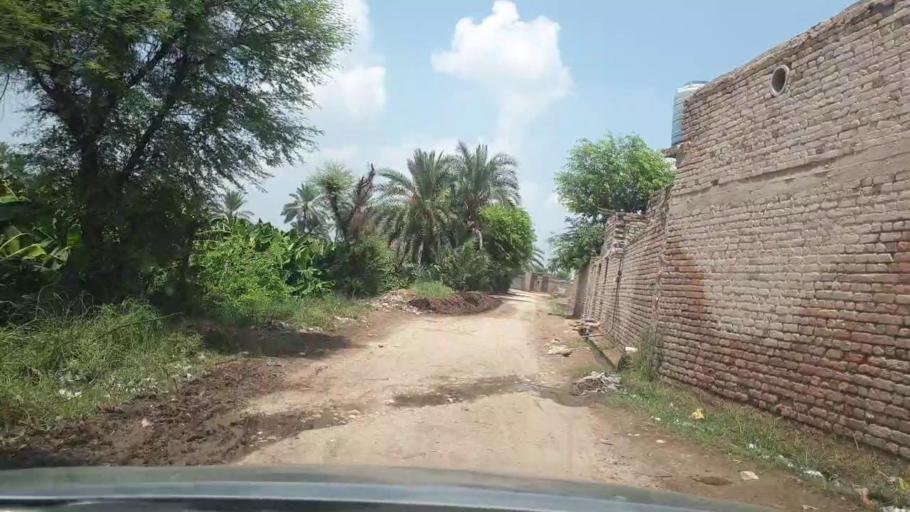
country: PK
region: Sindh
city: Pir jo Goth
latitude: 27.6091
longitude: 68.6130
